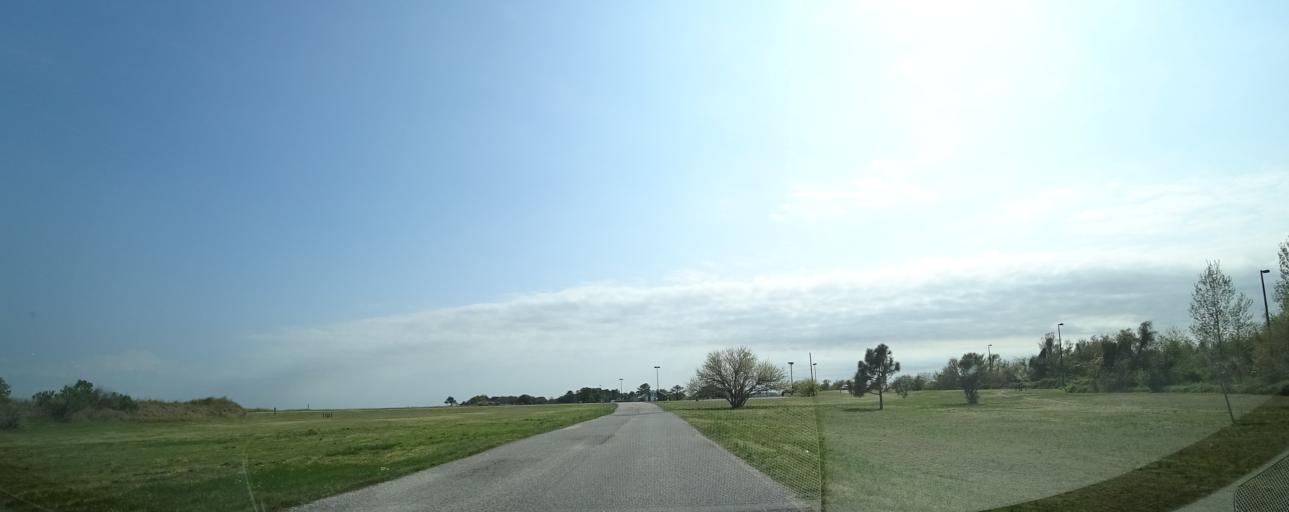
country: US
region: Virginia
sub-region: City of Hampton
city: East Hampton
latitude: 37.0262
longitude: -76.2968
